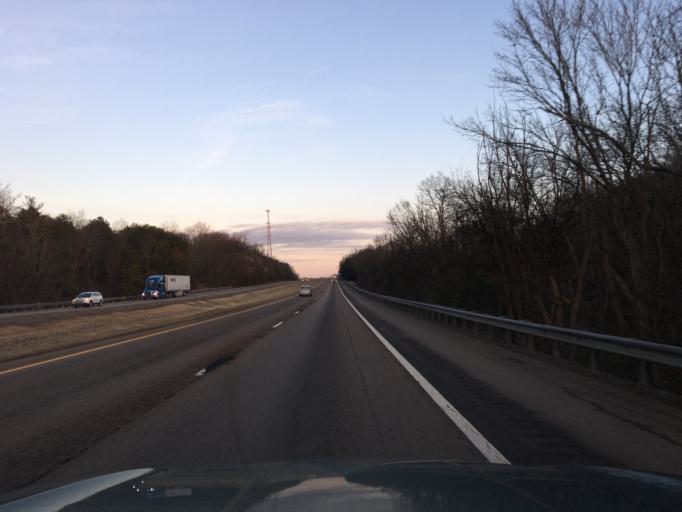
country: US
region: Tennessee
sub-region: Jefferson County
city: White Pine
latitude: 36.0117
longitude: -83.2937
